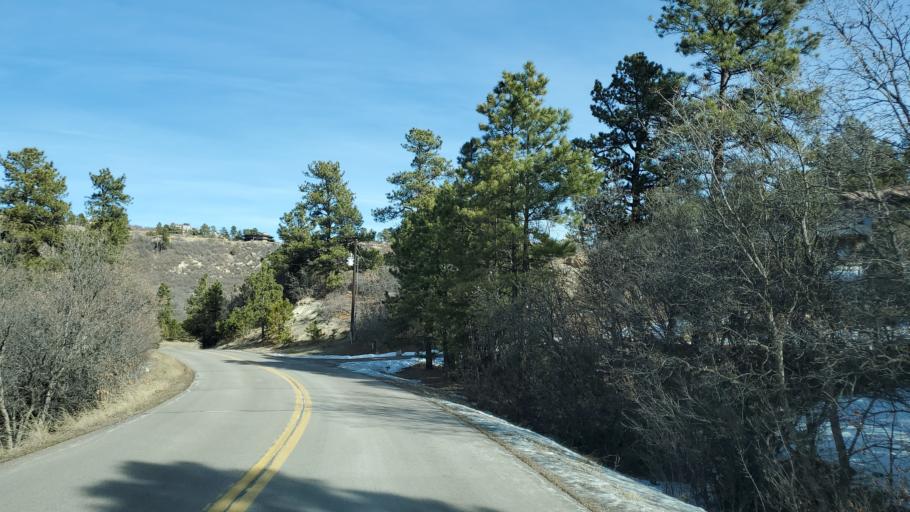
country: US
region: Colorado
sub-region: Douglas County
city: Castle Pines
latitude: 39.4318
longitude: -104.8705
